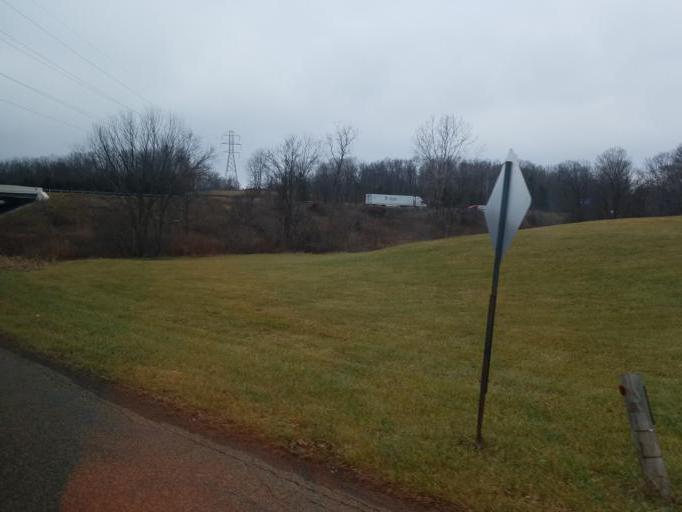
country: US
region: Ohio
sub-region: Richland County
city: Lexington
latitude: 40.6710
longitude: -82.5315
